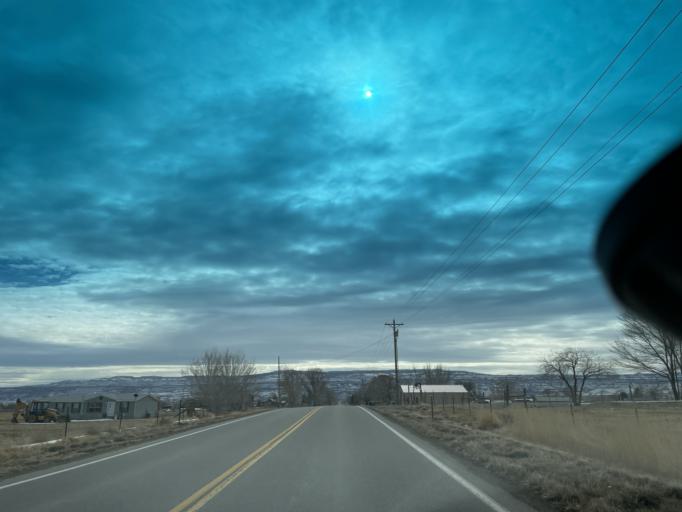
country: US
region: Colorado
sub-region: Mesa County
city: Loma
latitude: 39.2121
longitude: -108.8129
